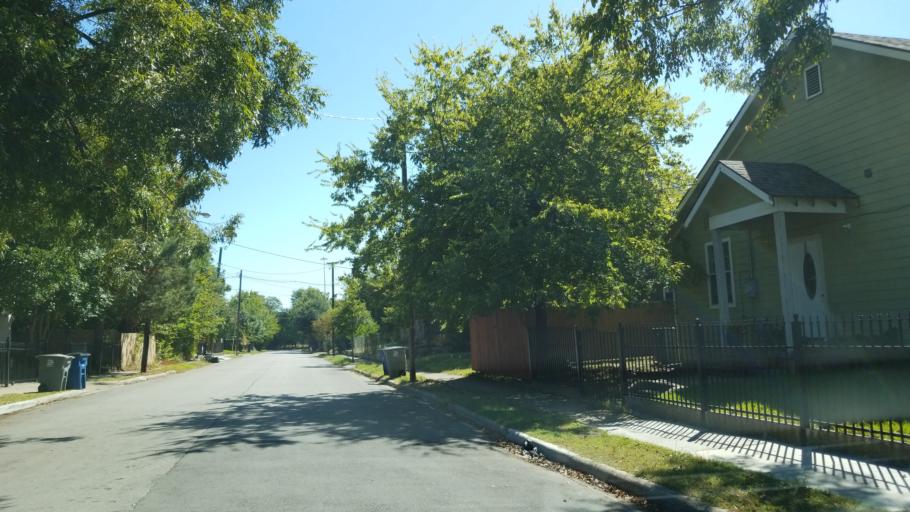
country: US
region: Texas
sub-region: Dallas County
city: Dallas
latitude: 32.7937
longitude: -96.7541
